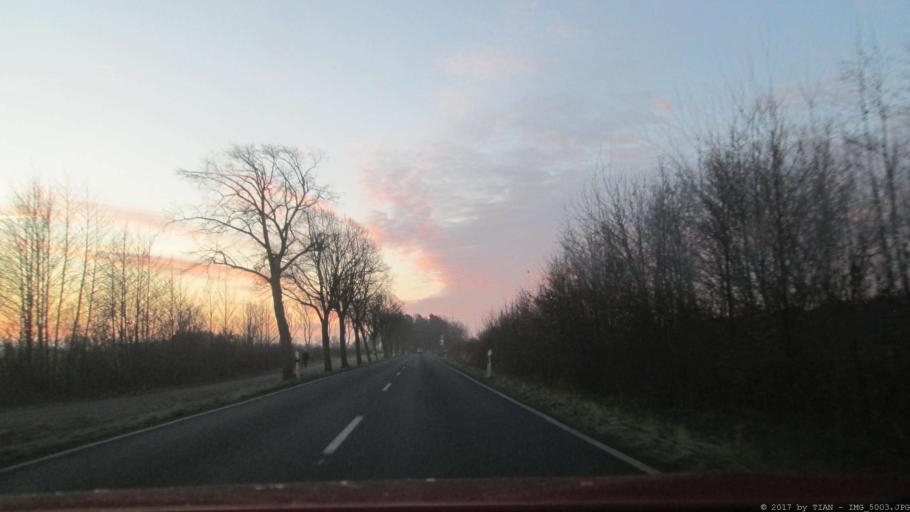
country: DE
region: Lower Saxony
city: Tiddische
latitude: 52.4663
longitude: 10.8207
